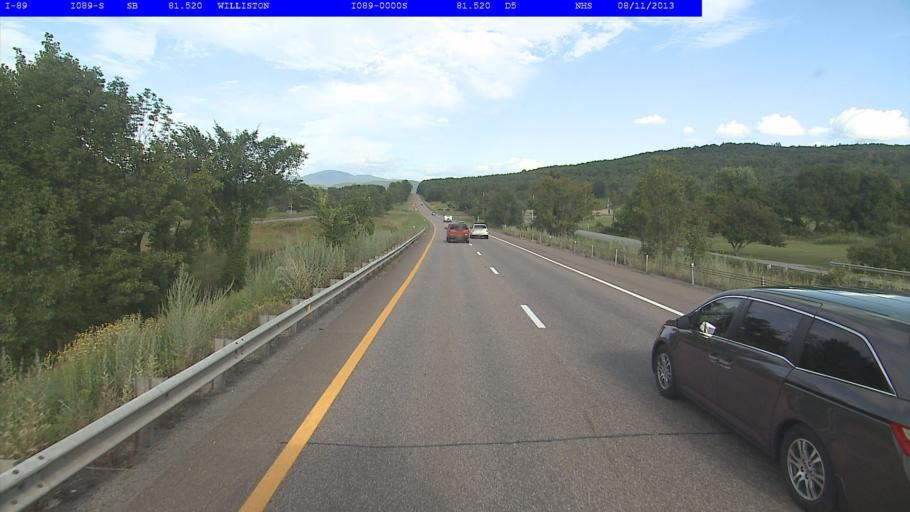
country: US
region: Vermont
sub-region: Chittenden County
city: Williston
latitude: 44.4334
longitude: -73.0666
